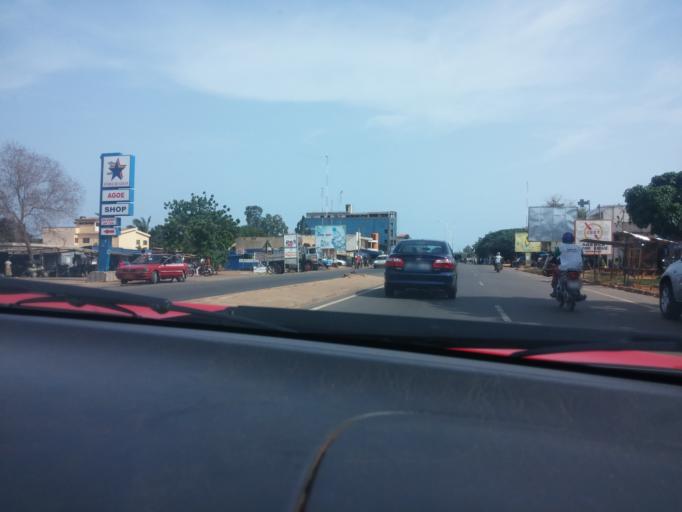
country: TG
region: Maritime
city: Lome
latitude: 6.2327
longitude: 1.2105
